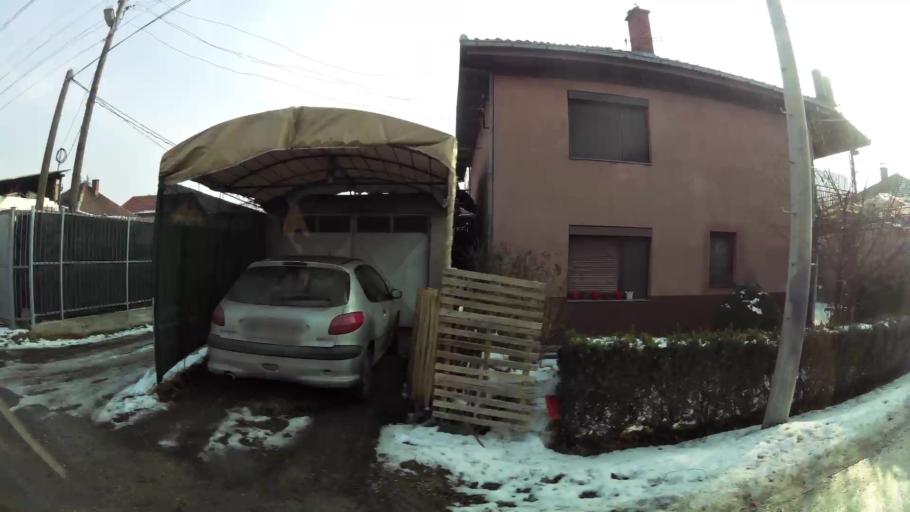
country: MK
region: Ilinden
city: Marino
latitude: 41.9892
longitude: 21.5861
